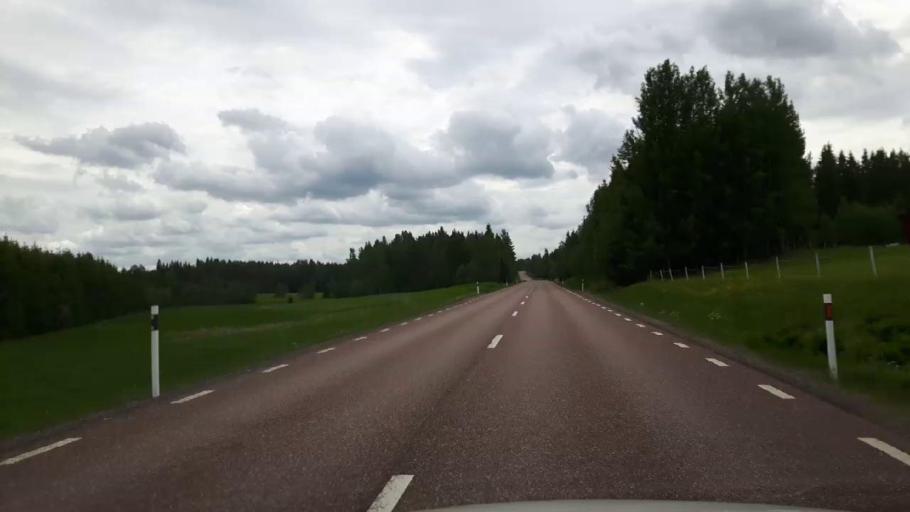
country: SE
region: Dalarna
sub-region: Hedemora Kommun
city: Brunna
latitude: 60.2034
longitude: 15.9935
